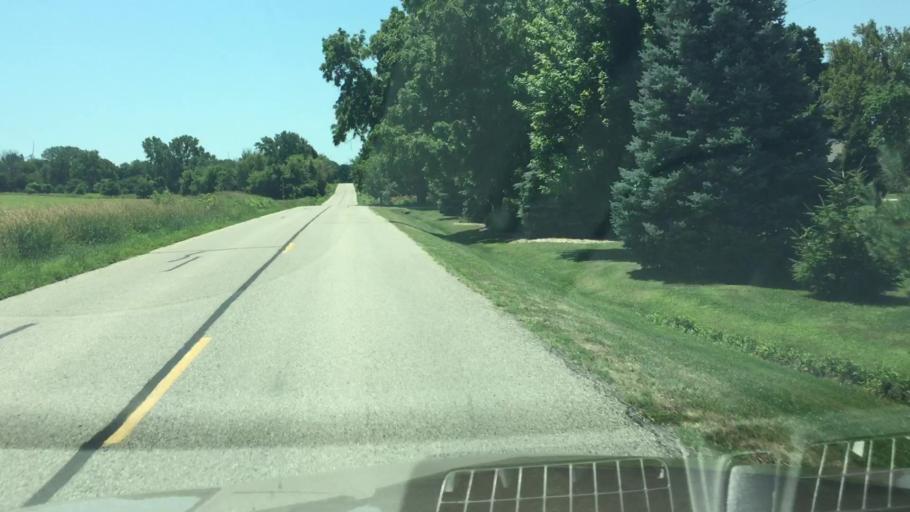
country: US
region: Wisconsin
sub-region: Fond du Lac County
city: Saint Peter
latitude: 43.9426
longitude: -88.3113
